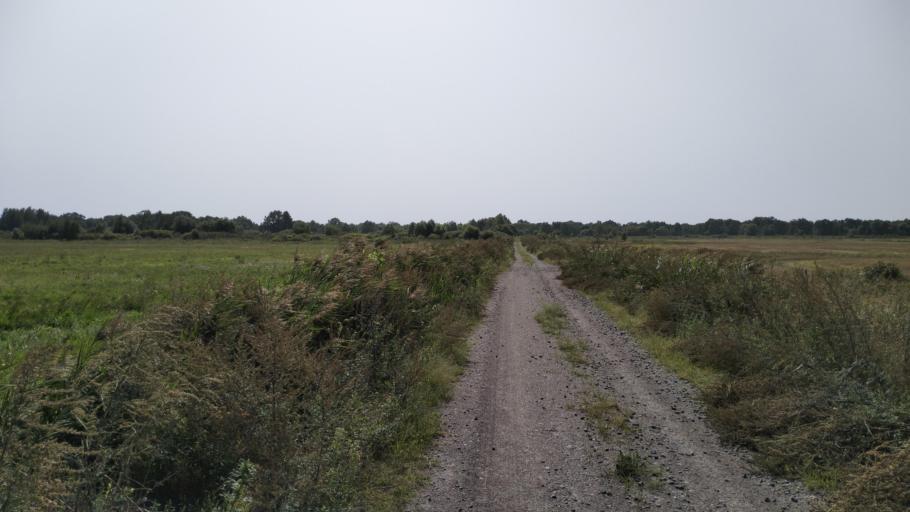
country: BY
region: Brest
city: Davyd-Haradok
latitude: 51.9708
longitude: 27.1738
